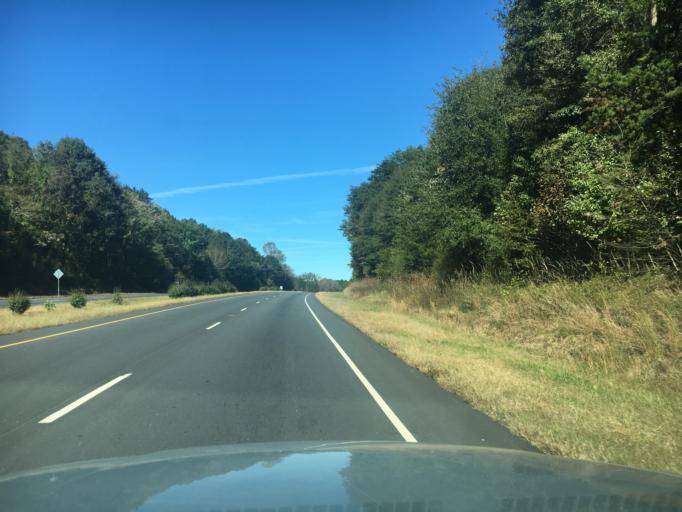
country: US
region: North Carolina
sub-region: Rutherford County
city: Spindale
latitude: 35.3502
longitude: -81.9396
